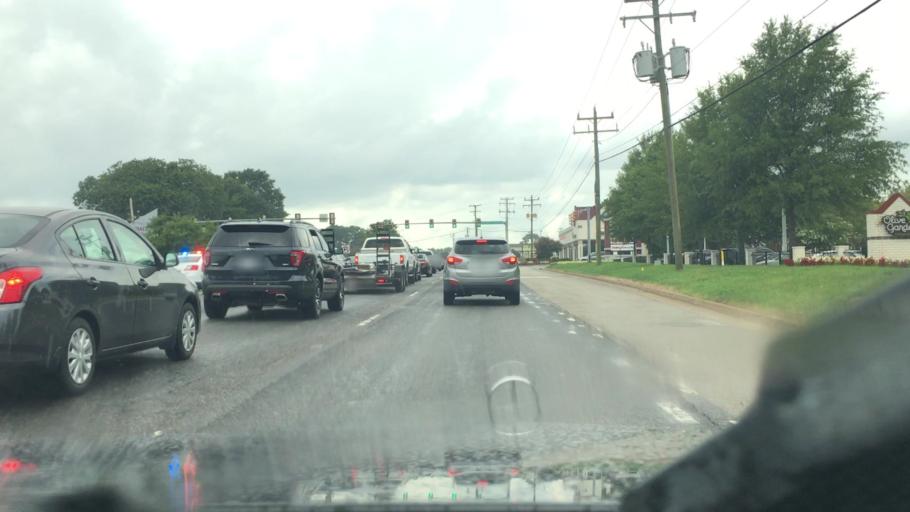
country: US
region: Virginia
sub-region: Chesterfield County
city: Bon Air
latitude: 37.5031
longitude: -77.5752
